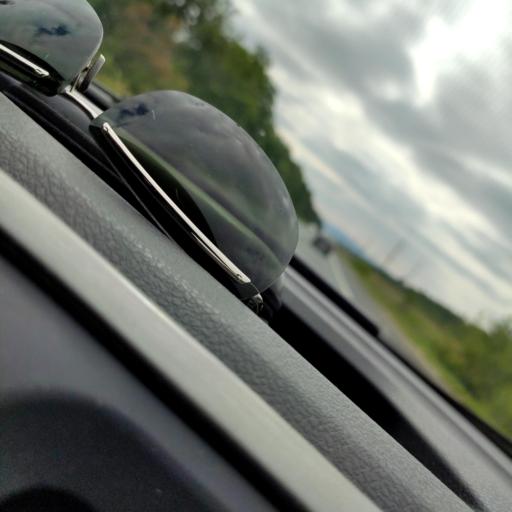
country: RU
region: Samara
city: Bogatyr'
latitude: 53.5061
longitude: 49.9392
